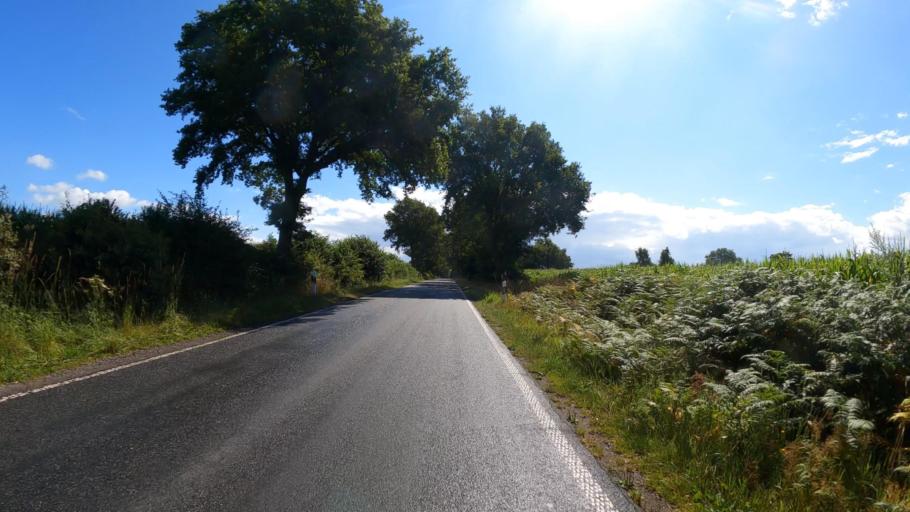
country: DE
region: Schleswig-Holstein
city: Armstedt
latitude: 53.9605
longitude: 9.8604
